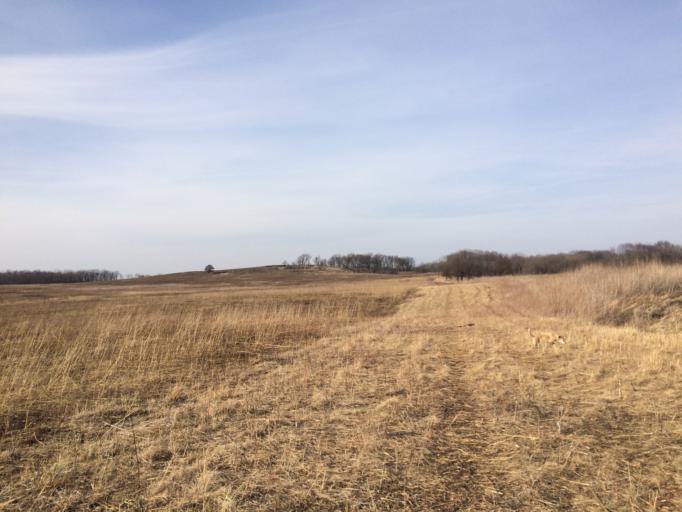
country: US
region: Illinois
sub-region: Cook County
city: Streamwood
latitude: 42.0542
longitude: -88.1985
